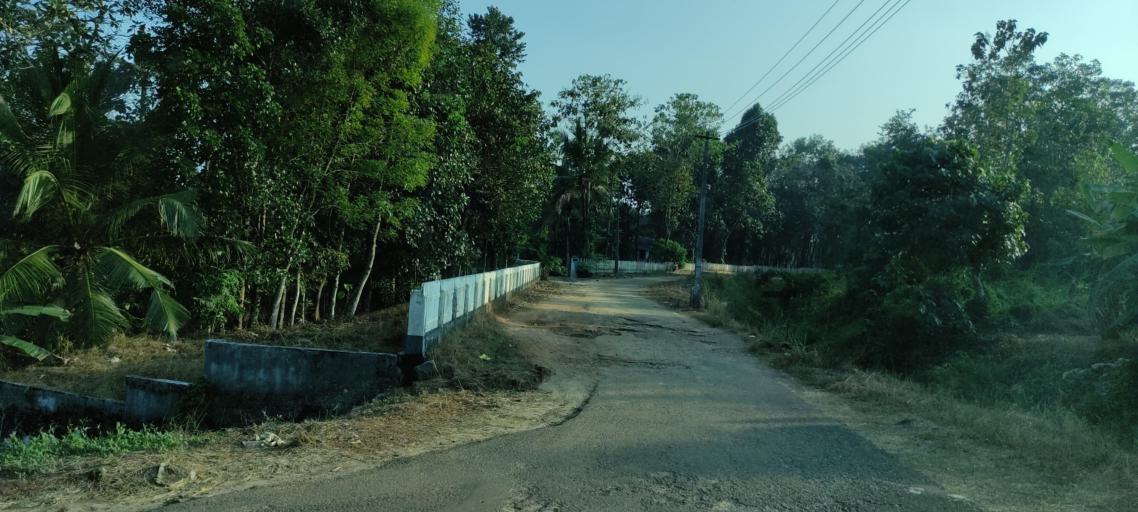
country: IN
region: Kerala
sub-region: Pattanamtitta
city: Adur
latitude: 9.1359
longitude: 76.7338
